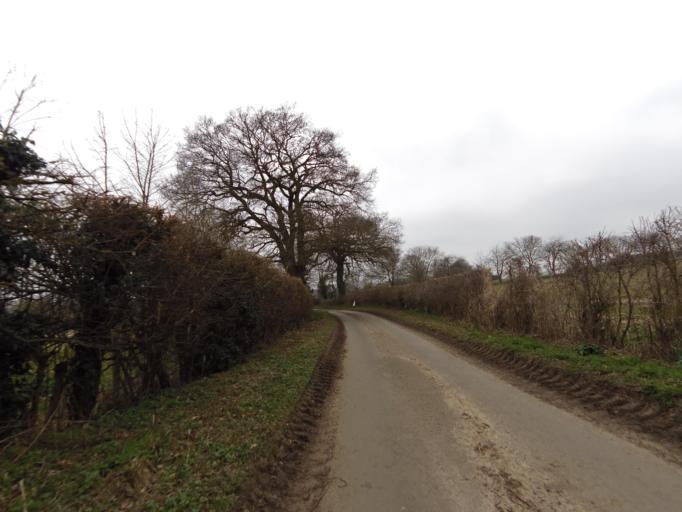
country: GB
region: England
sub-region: Suffolk
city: Framlingham
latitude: 52.2459
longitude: 1.4019
